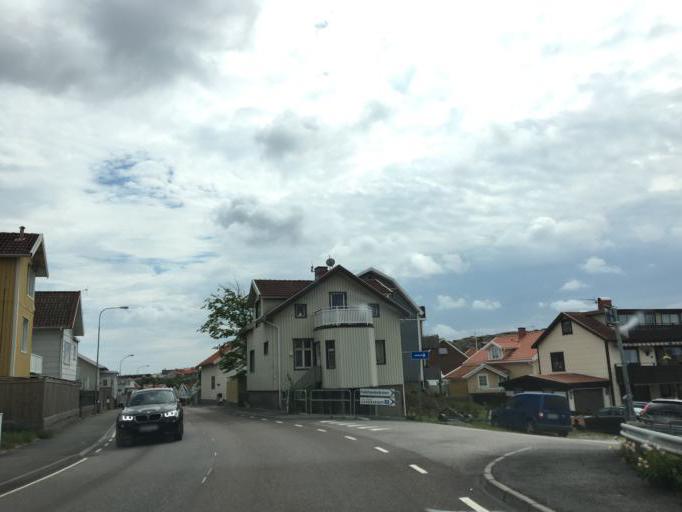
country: SE
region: Vaestra Goetaland
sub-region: Sotenas Kommun
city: Kungshamn
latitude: 58.3647
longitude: 11.2492
